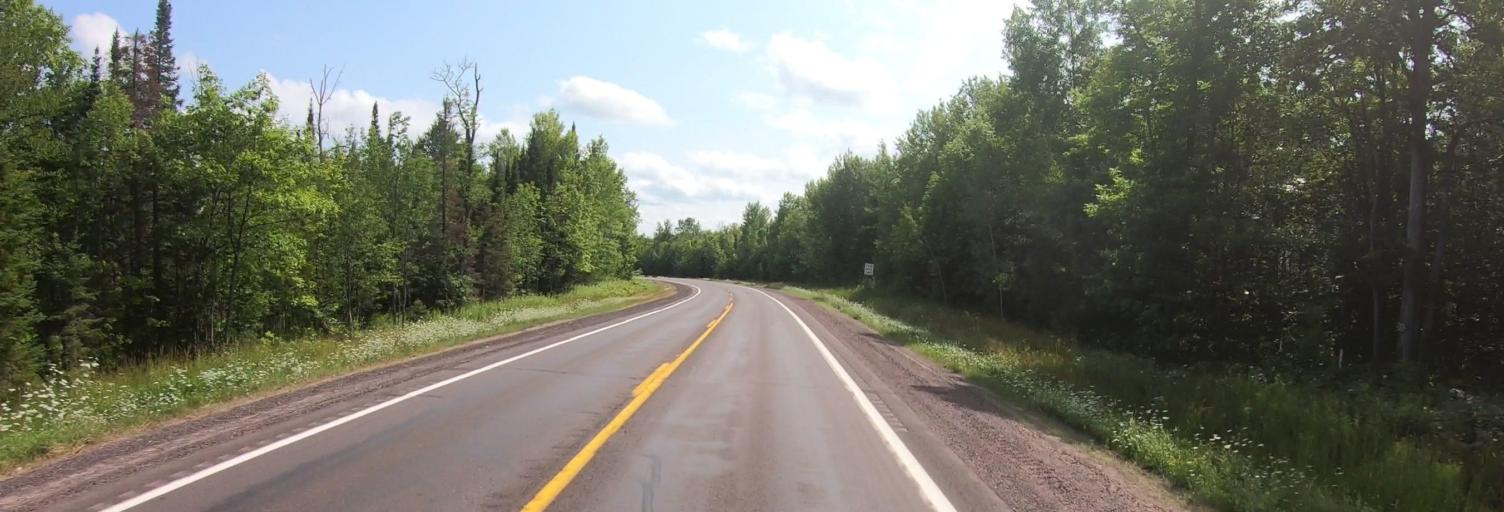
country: US
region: Michigan
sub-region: Ontonagon County
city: Ontonagon
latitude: 46.8290
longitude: -88.9969
